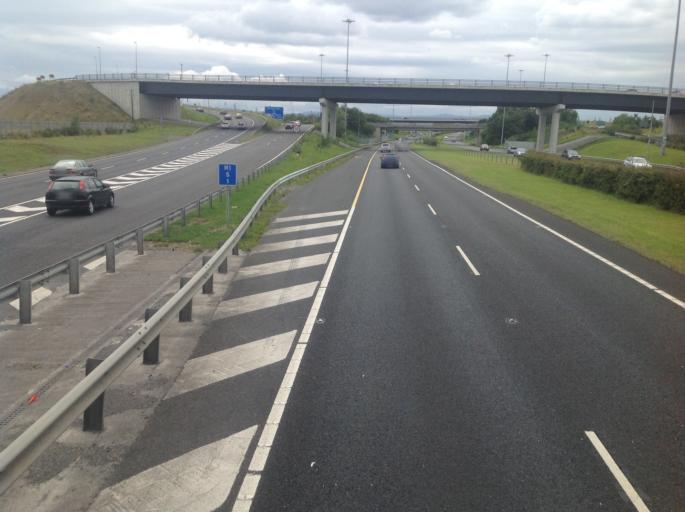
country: IE
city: Bonnybrook
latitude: 53.4134
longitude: -6.2247
